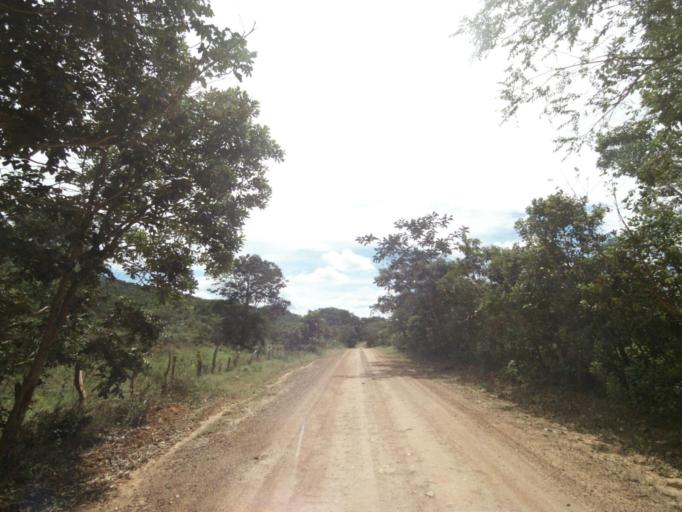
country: BR
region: Goias
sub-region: Pirenopolis
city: Pirenopolis
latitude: -15.7913
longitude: -48.8870
